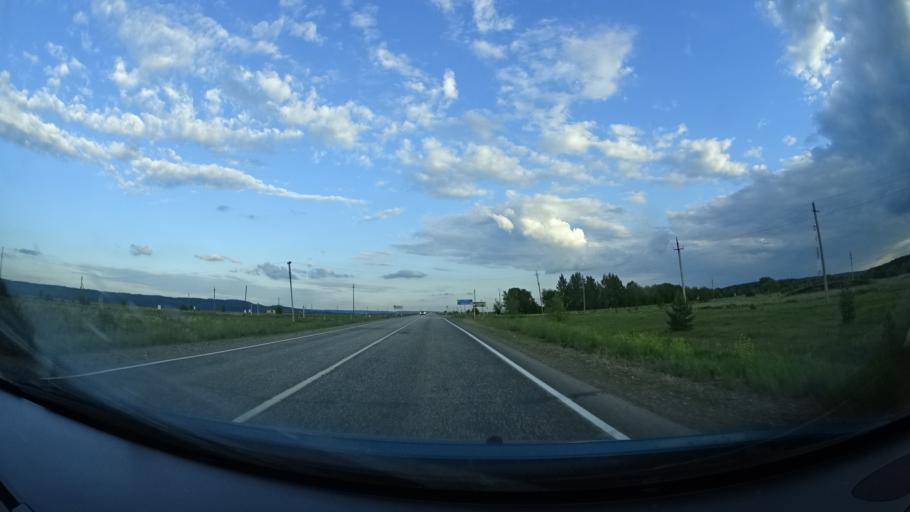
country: RU
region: Perm
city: Barda
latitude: 56.9960
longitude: 55.5703
